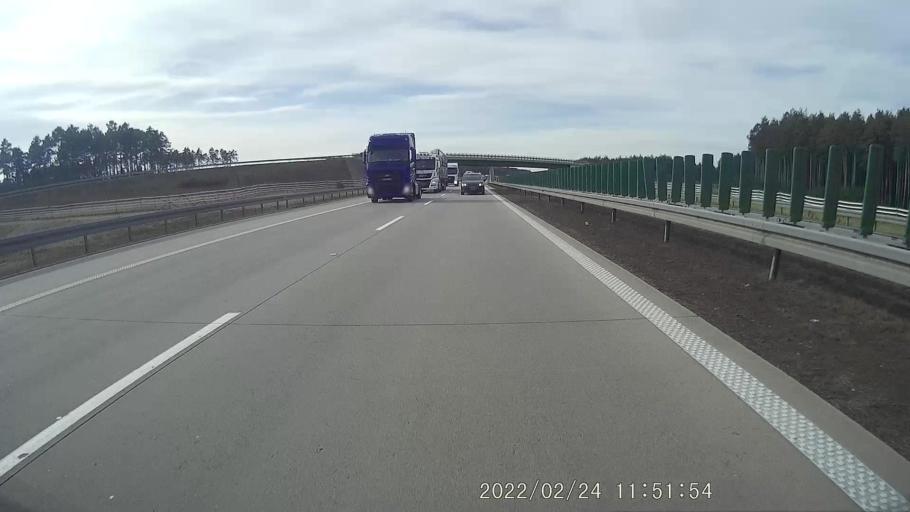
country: PL
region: Lower Silesian Voivodeship
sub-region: Powiat polkowicki
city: Radwanice
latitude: 51.6171
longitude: 15.9719
